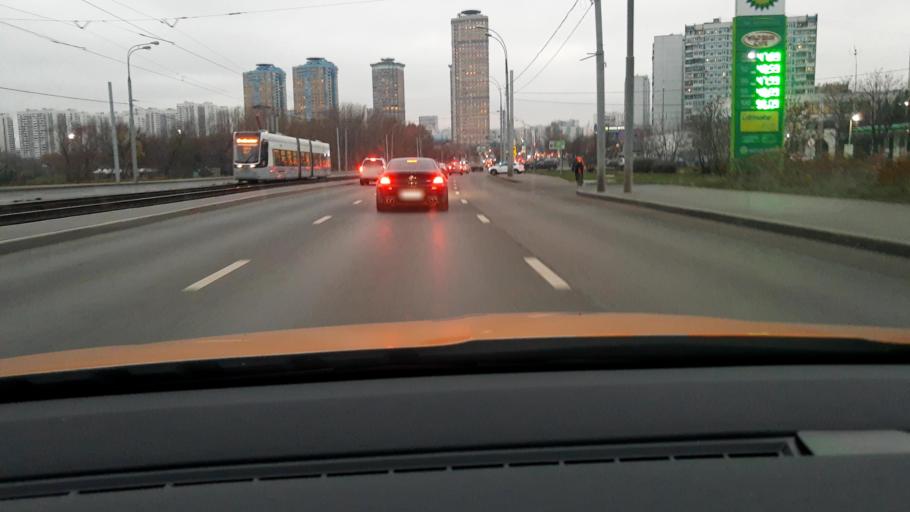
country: RU
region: Moscow
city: Strogino
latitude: 55.8031
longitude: 37.4273
